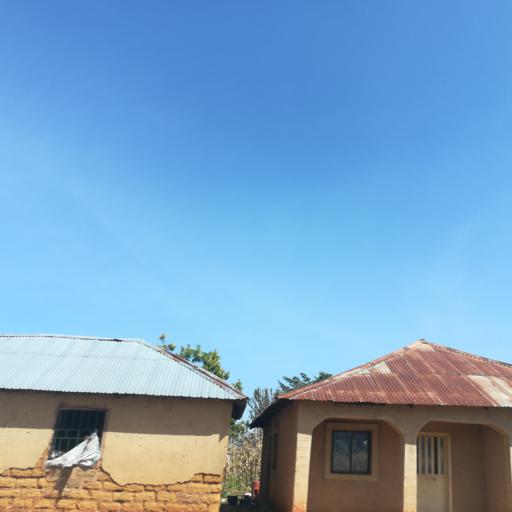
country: NG
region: Plateau
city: Bukuru
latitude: 9.7574
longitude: 8.8734
